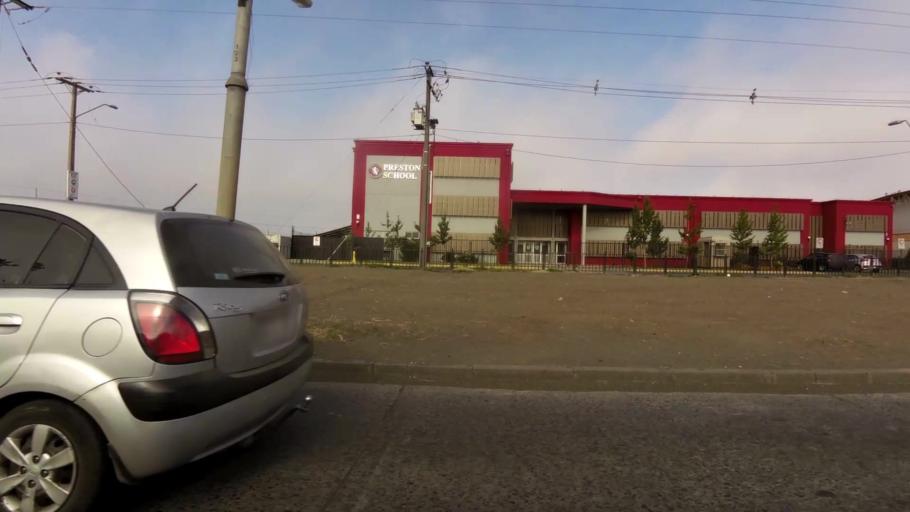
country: CL
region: Biobio
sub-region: Provincia de Concepcion
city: Concepcion
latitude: -36.7986
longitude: -73.1062
